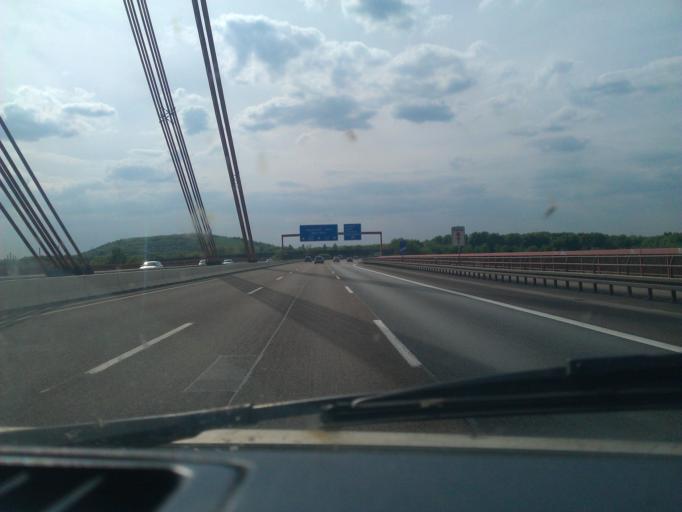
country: DE
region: North Rhine-Westphalia
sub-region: Regierungsbezirk Dusseldorf
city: Moers
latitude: 51.4810
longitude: 6.6783
